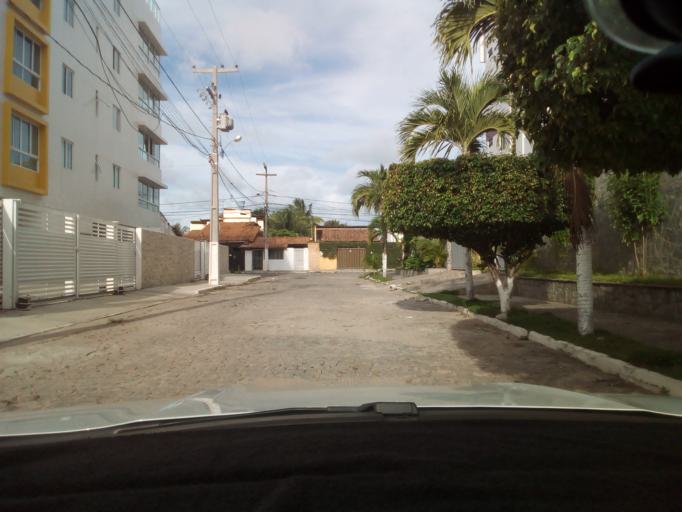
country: BR
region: Paraiba
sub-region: Cabedelo
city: Cabedelo
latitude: -7.0231
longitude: -34.8309
